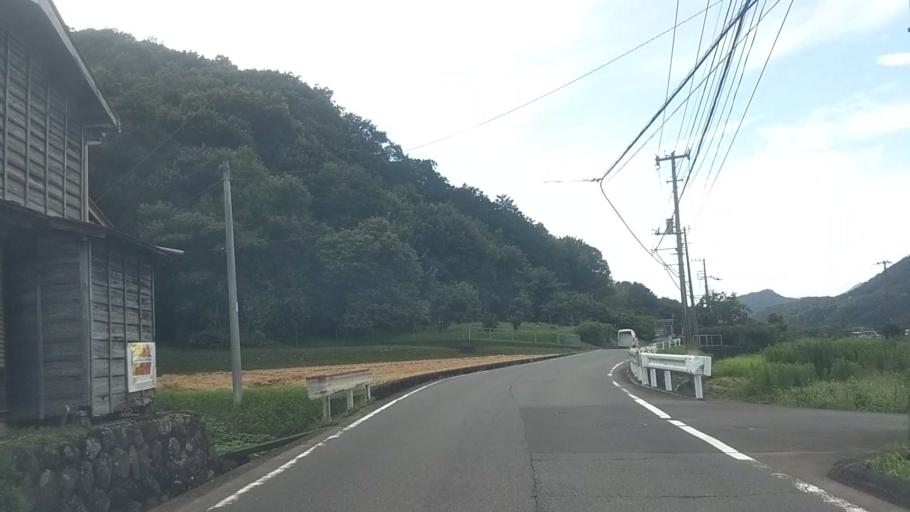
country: JP
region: Shizuoka
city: Ito
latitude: 34.9684
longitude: 138.9669
